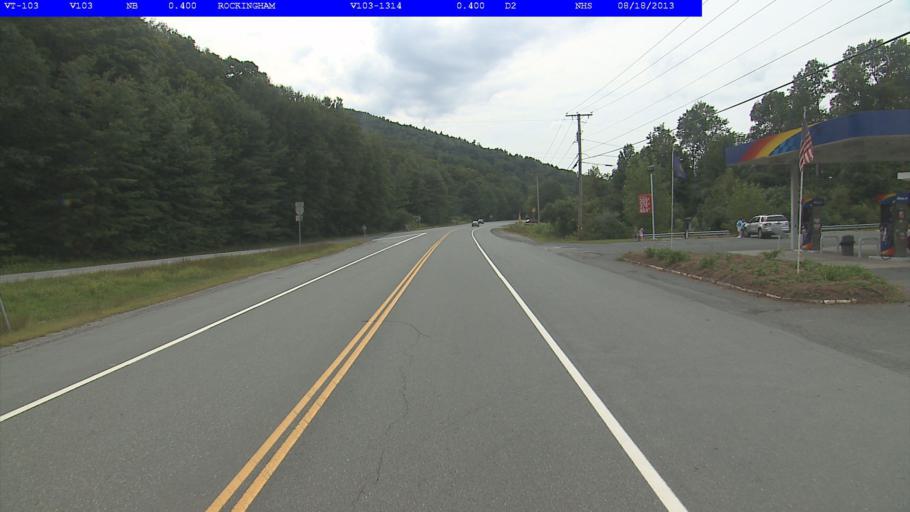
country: US
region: Vermont
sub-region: Windham County
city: Rockingham
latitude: 43.1793
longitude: -72.4670
